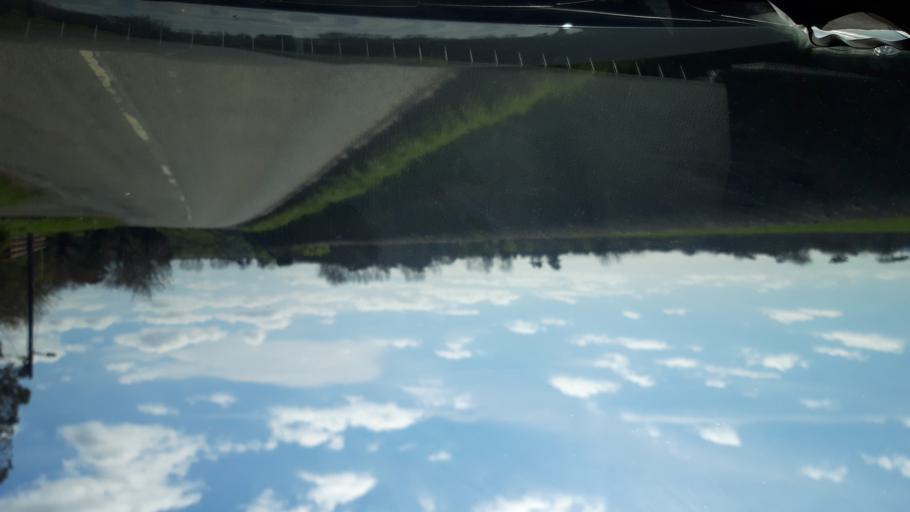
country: IE
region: Leinster
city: Malahide
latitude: 53.4280
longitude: -6.1683
